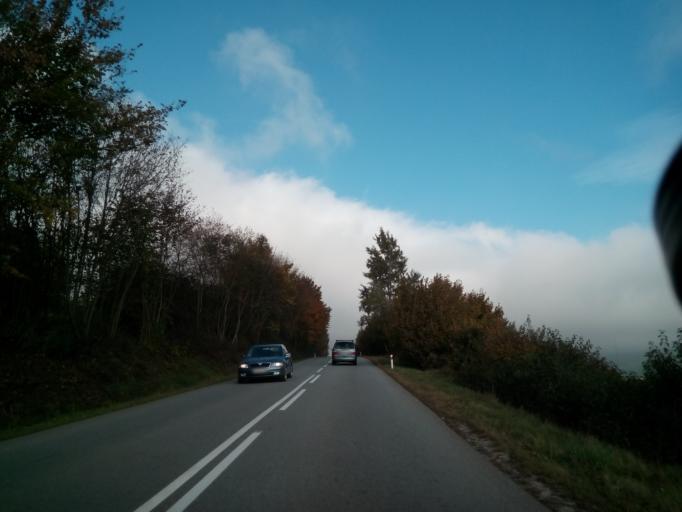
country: SK
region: Kosicky
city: Gelnica
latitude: 48.9142
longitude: 20.9358
